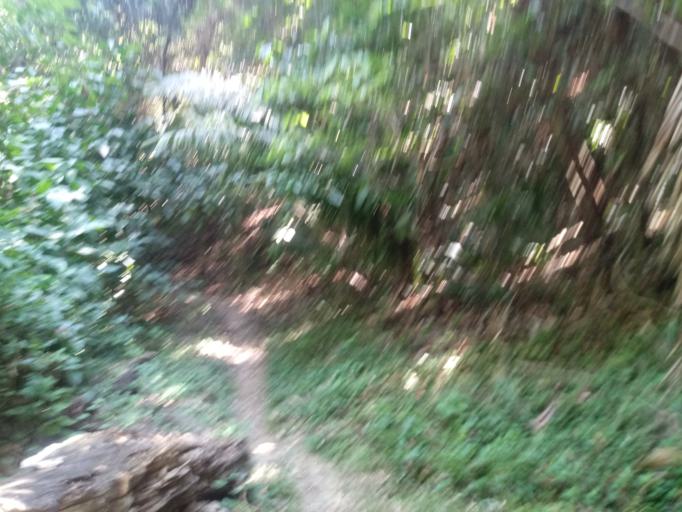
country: CR
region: Puntarenas
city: Paquera
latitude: 9.5853
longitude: -85.0970
